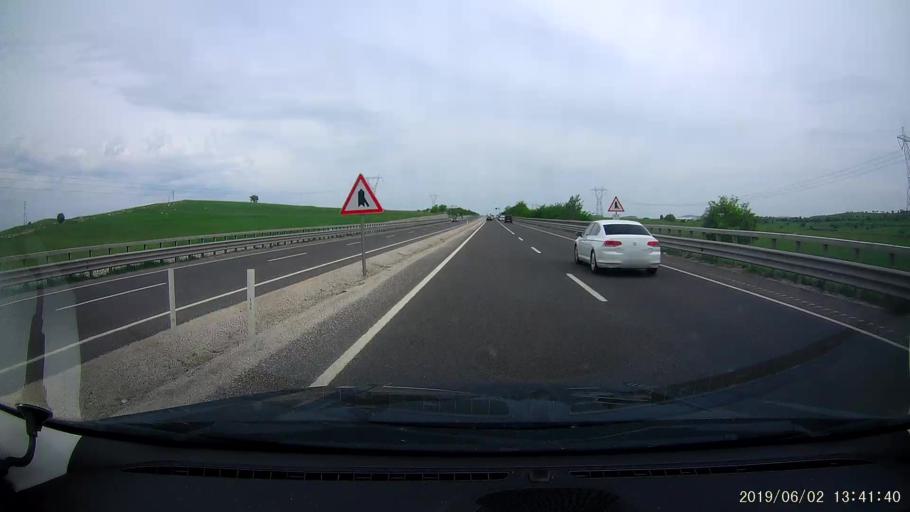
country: TR
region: Cankiri
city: Kursunlu
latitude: 40.8430
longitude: 33.1811
